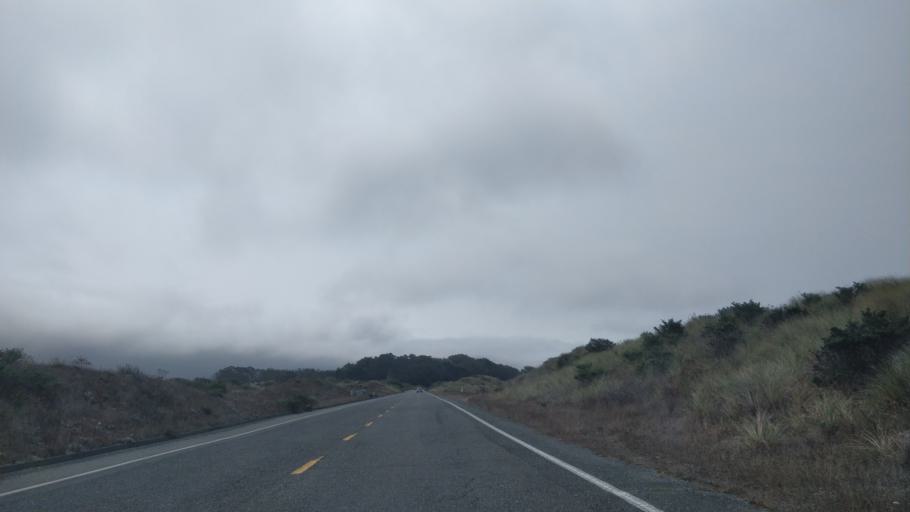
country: US
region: California
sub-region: Humboldt County
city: Bayview
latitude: 40.7866
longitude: -124.2068
